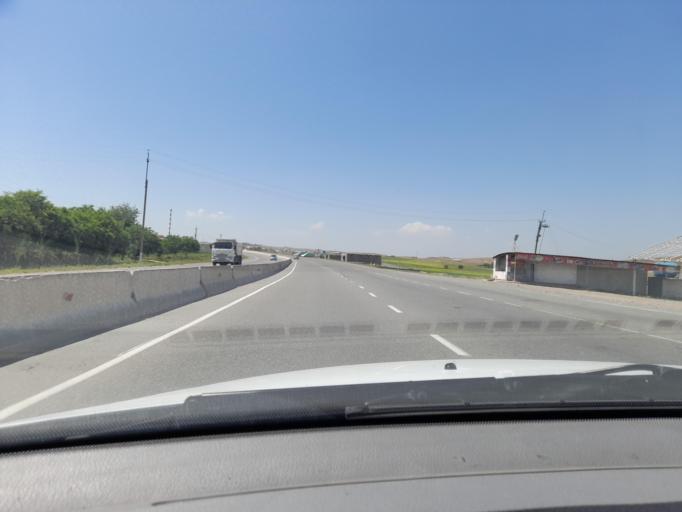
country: UZ
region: Jizzax
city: Jizzax
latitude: 40.0659
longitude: 67.8490
